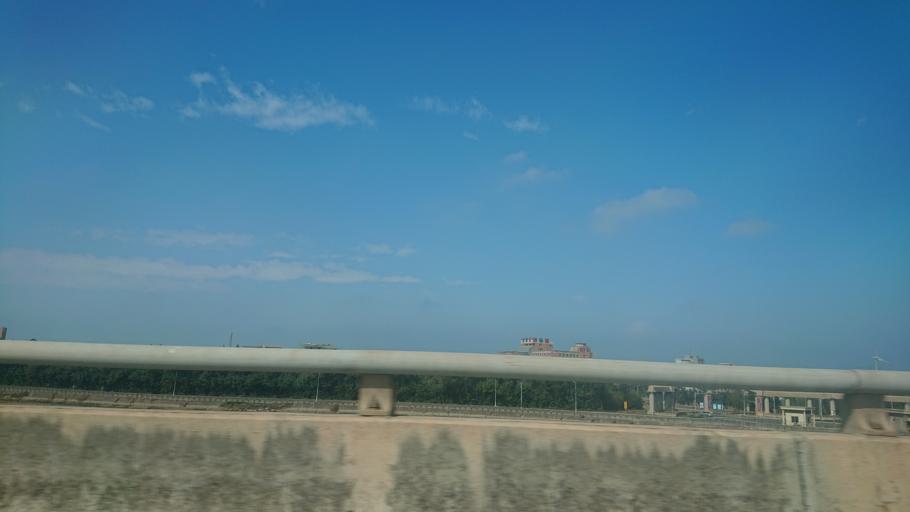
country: TW
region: Taiwan
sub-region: Changhua
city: Chang-hua
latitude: 24.0762
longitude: 120.4167
